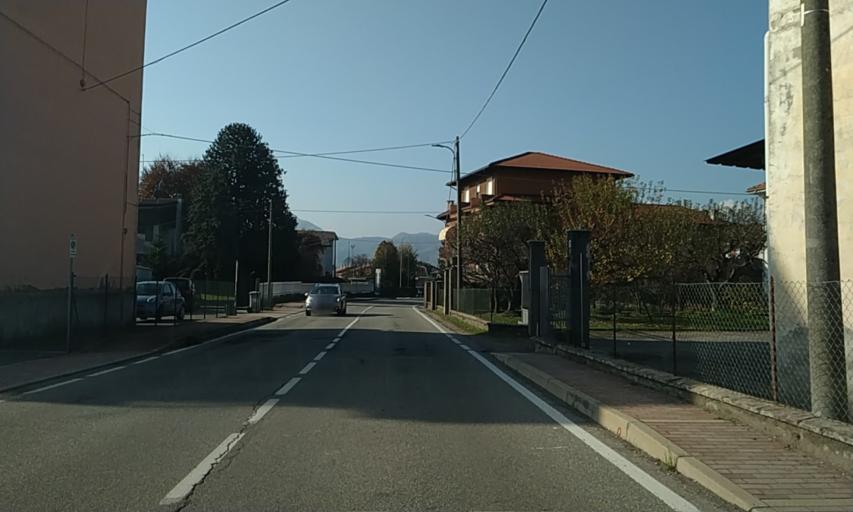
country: IT
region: Piedmont
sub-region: Provincia di Novara
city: Grignasco
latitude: 45.6814
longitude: 8.3479
